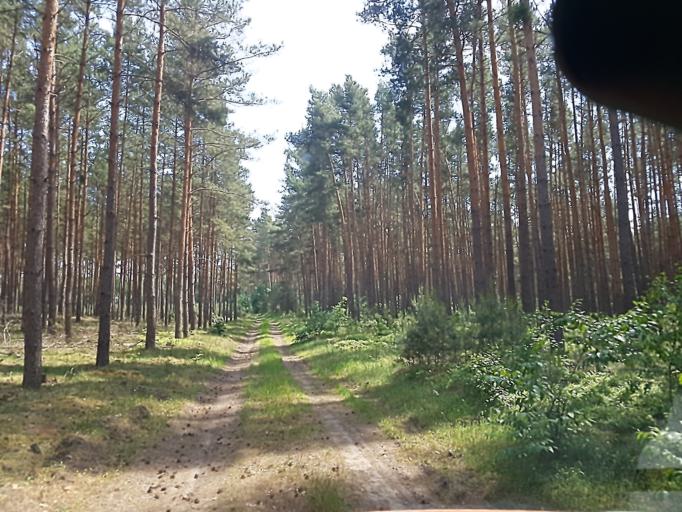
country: DE
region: Brandenburg
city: Gorzke
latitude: 52.1009
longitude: 12.2998
